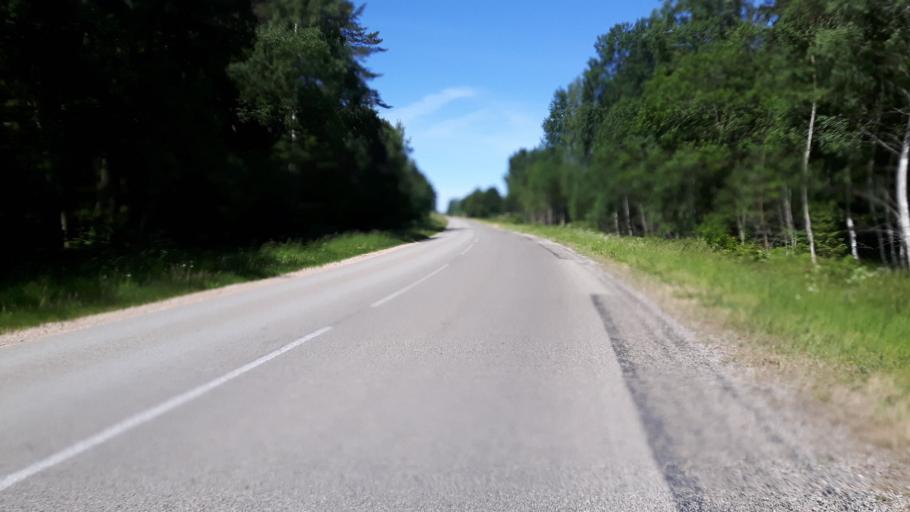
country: LV
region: Tukuma Rajons
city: Tukums
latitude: 57.0163
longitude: 23.0431
